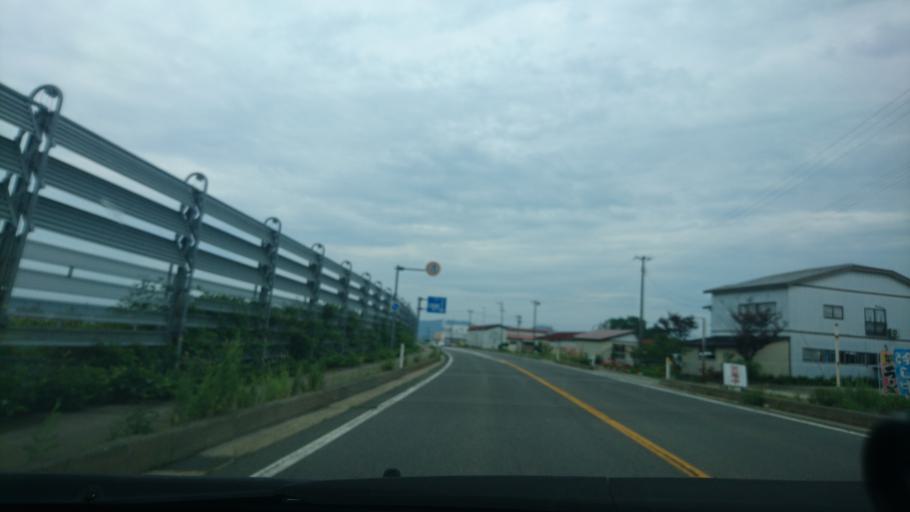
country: JP
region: Akita
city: Omagari
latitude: 39.4209
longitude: 140.5370
